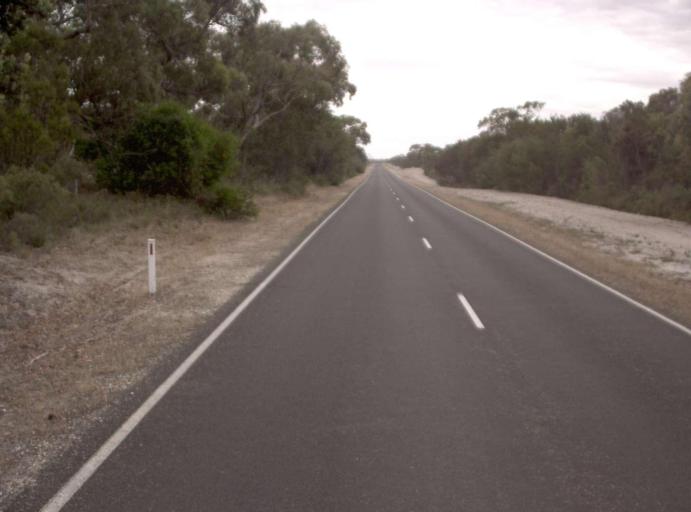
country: AU
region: Victoria
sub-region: Wellington
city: Sale
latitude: -38.1793
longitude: 147.3785
